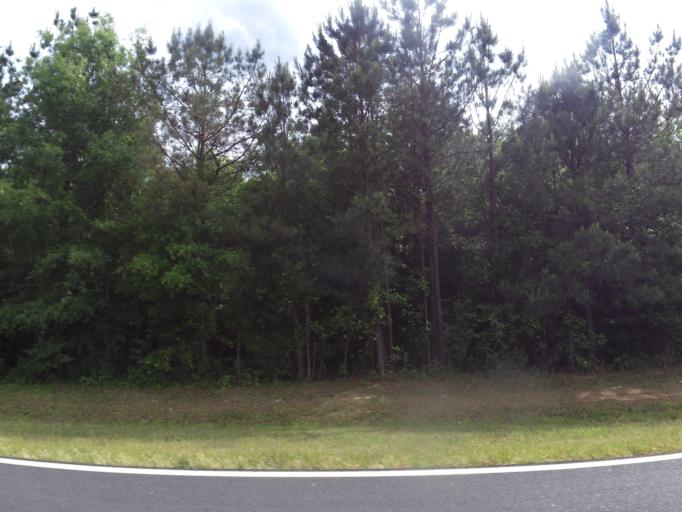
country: US
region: Georgia
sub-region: McDuffie County
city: Thomson
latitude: 33.5374
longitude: -82.4982
